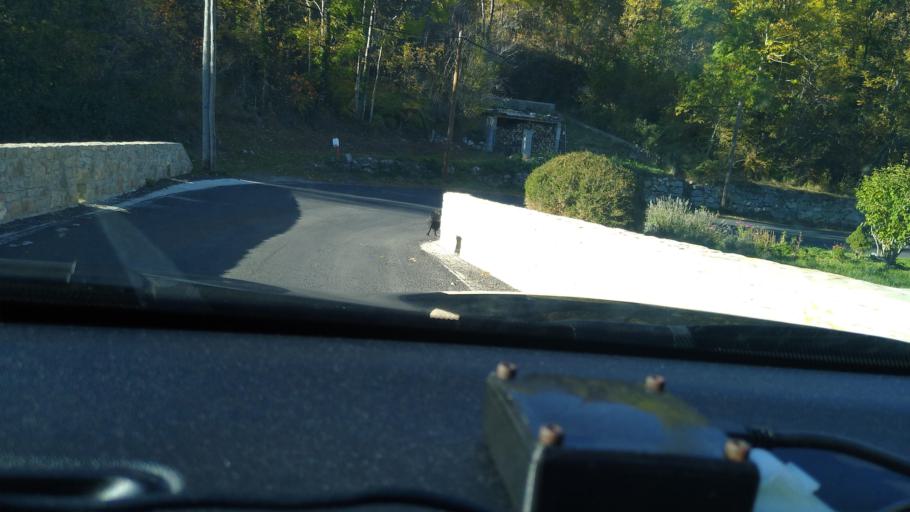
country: FR
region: Languedoc-Roussillon
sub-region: Departement de l'Aude
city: Quillan
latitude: 42.7447
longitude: 2.1637
